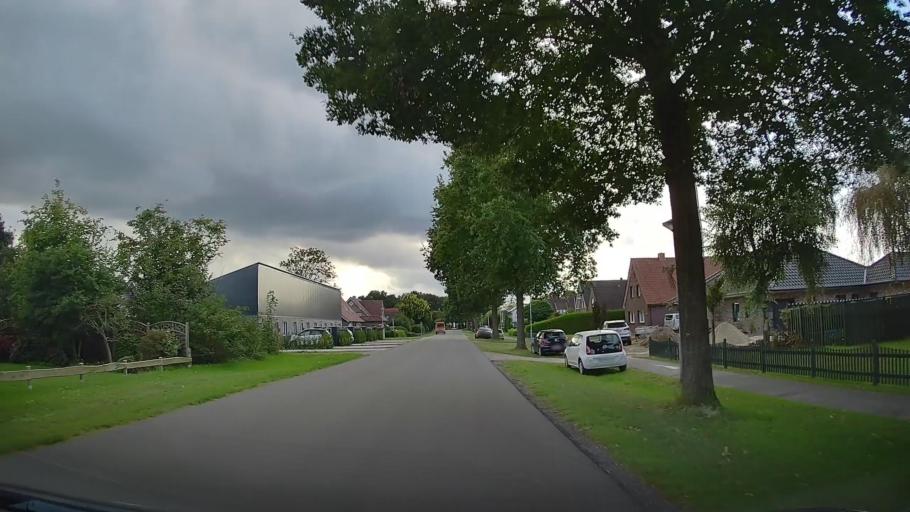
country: DE
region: Lower Saxony
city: Hilkenbrook
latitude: 53.0484
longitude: 7.7397
